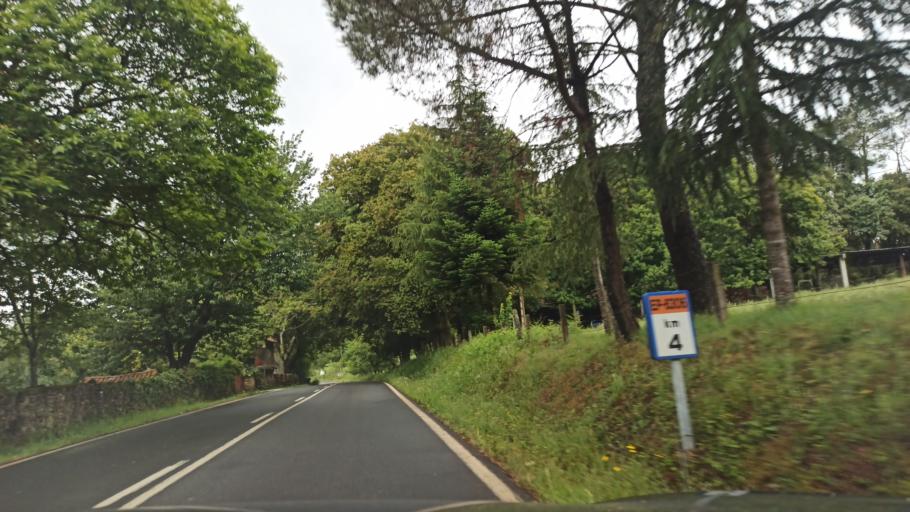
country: ES
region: Galicia
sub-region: Provincia da Coruna
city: Santiso
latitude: 42.7852
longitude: -8.0581
